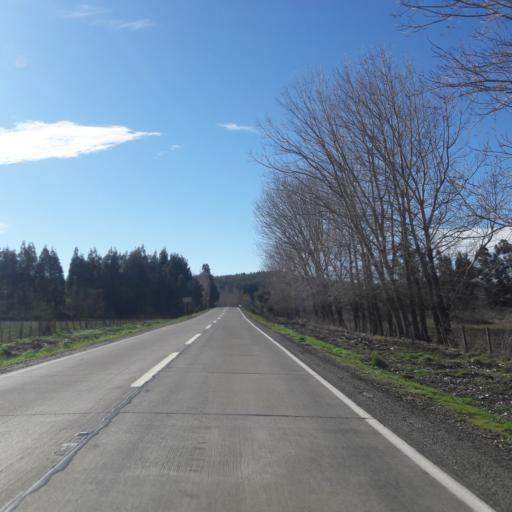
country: CL
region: Araucania
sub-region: Provincia de Malleco
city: Collipulli
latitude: -37.7839
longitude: -72.5221
